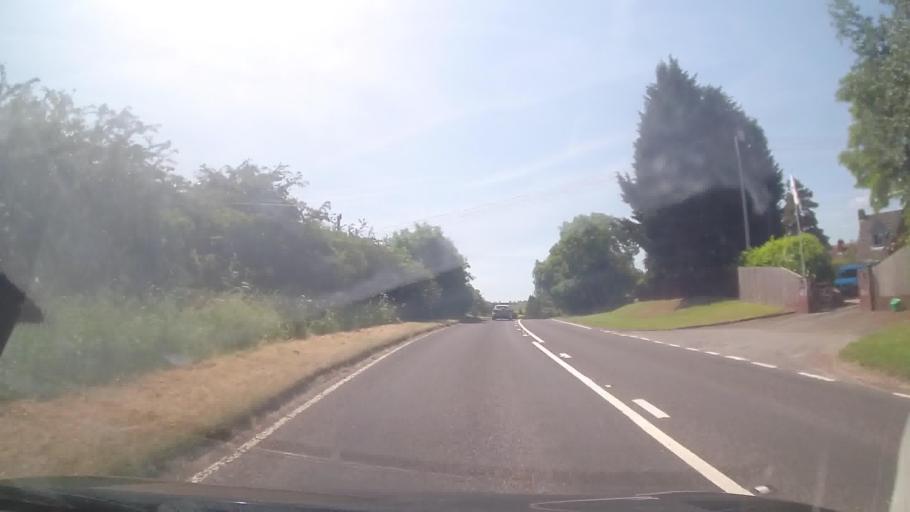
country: GB
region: England
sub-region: Herefordshire
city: Wellington
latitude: 52.0970
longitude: -2.7292
